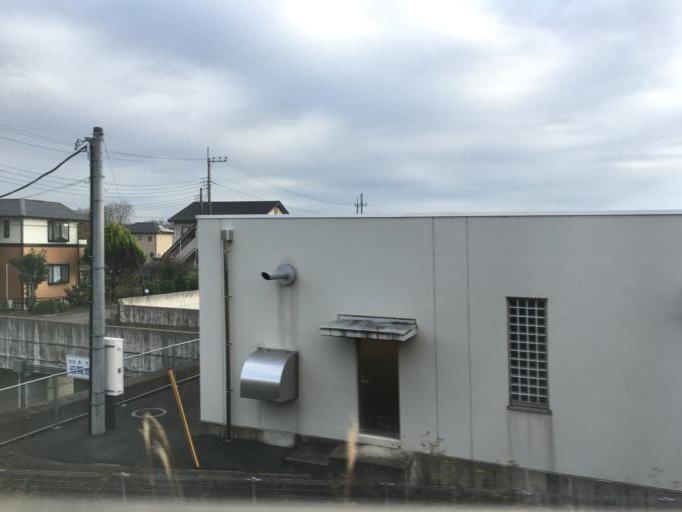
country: JP
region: Tochigi
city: Ashikaga
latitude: 36.3145
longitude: 139.5145
